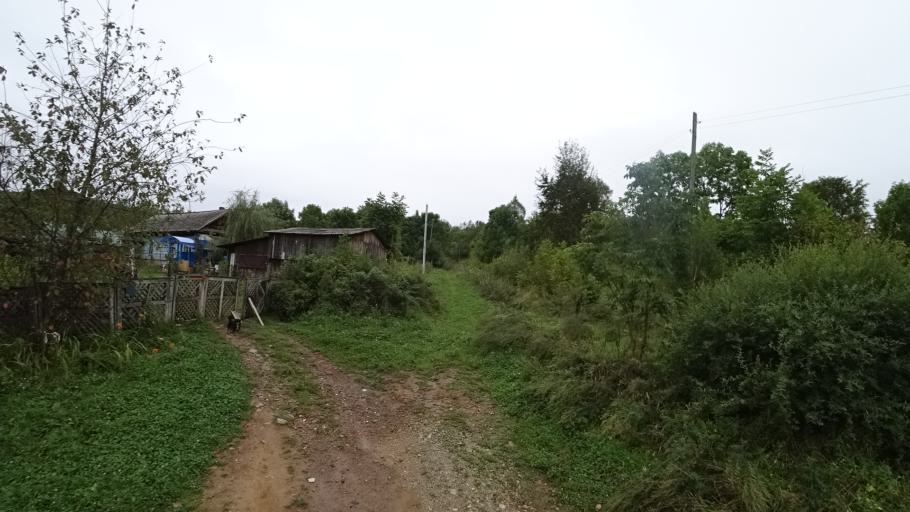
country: RU
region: Primorskiy
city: Rettikhovka
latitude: 44.1744
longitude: 132.8891
